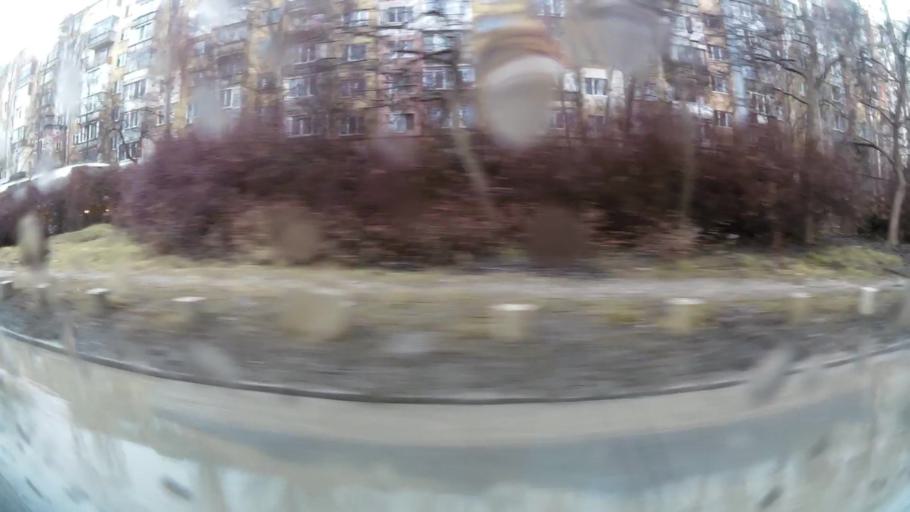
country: BG
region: Sofia-Capital
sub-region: Stolichna Obshtina
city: Sofia
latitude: 42.6690
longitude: 23.4004
